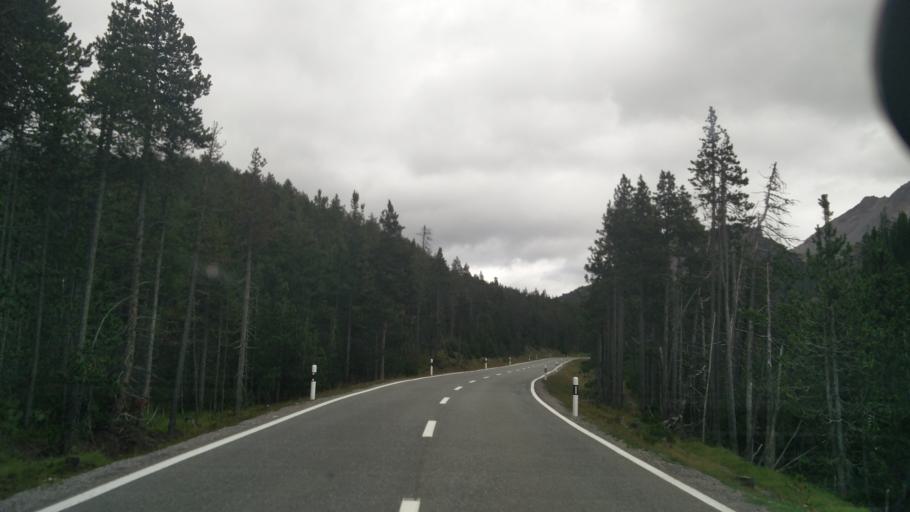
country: CH
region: Grisons
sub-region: Inn District
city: Scuol
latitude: 46.6510
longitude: 10.2615
